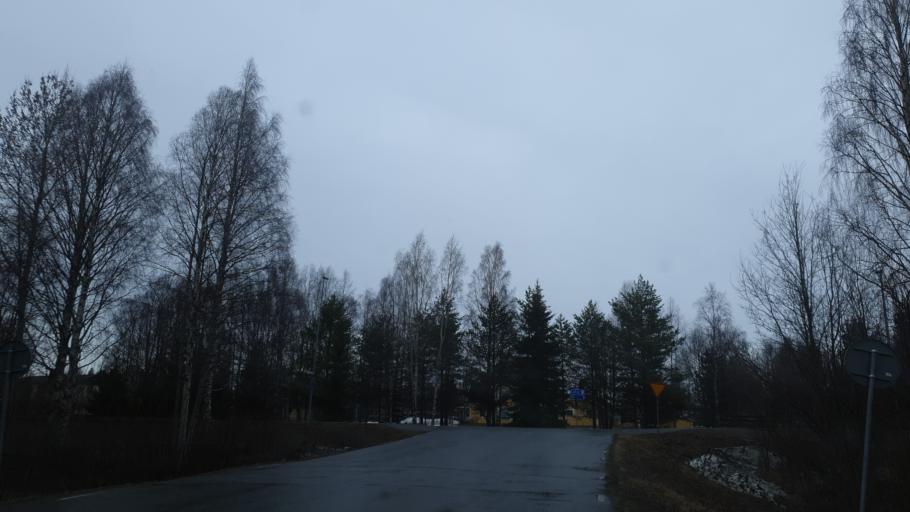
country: SE
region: Vaesterbotten
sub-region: Skelleftea Kommun
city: Kage
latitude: 64.8377
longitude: 20.9884
